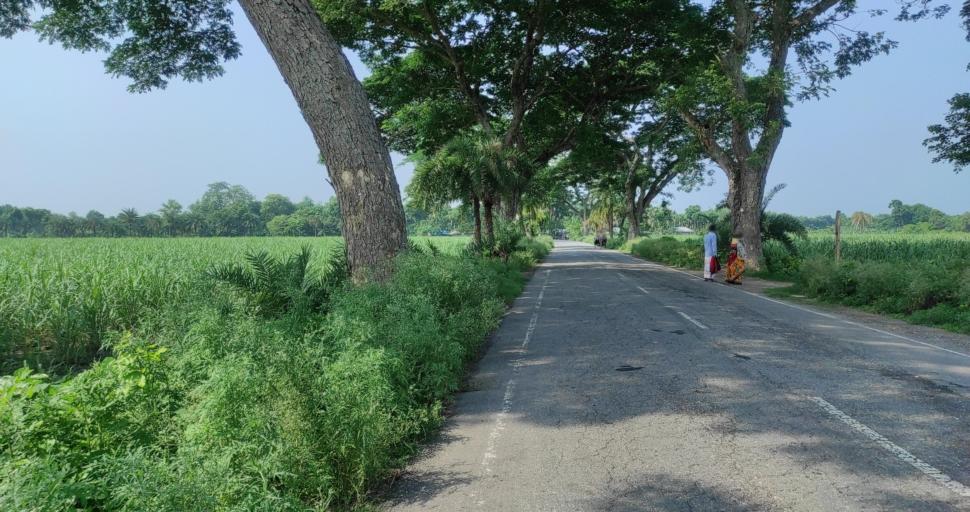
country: BD
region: Rajshahi
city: Ishurdi
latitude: 24.2638
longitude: 89.0502
